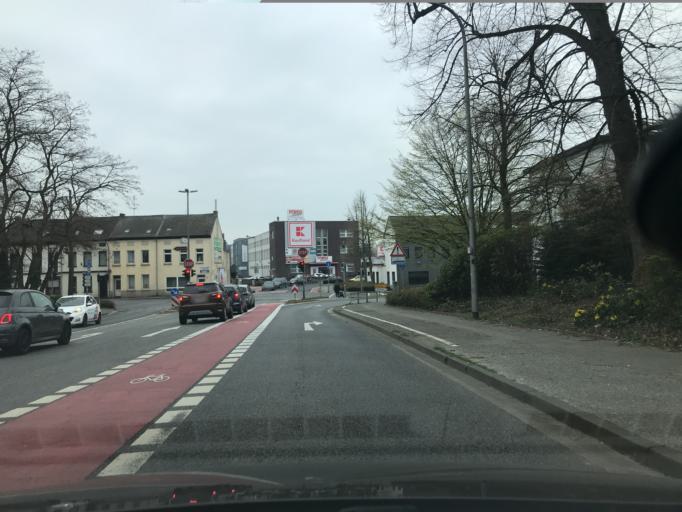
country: DE
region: North Rhine-Westphalia
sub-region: Regierungsbezirk Dusseldorf
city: Viersen
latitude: 51.2533
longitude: 6.3289
